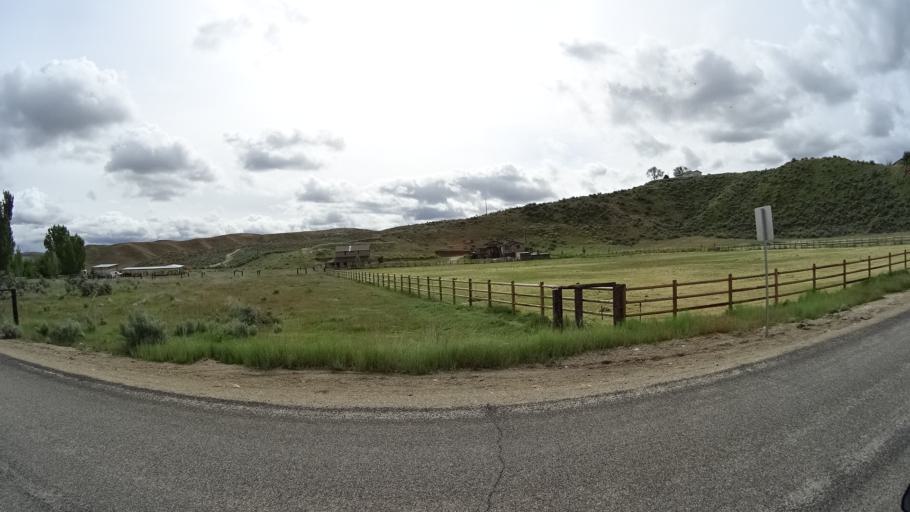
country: US
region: Idaho
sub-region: Ada County
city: Eagle
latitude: 43.7457
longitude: -116.3574
